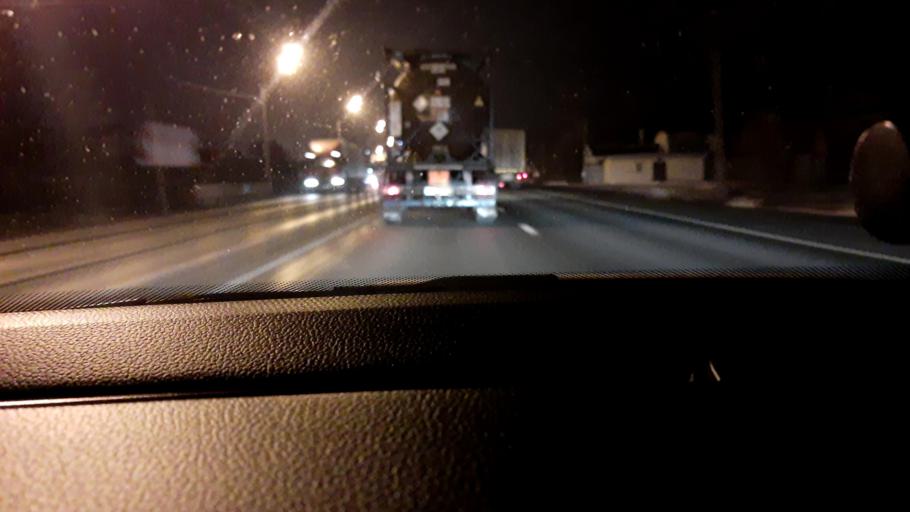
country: RU
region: Moskovskaya
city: Demikhovo
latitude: 55.8531
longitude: 38.8637
